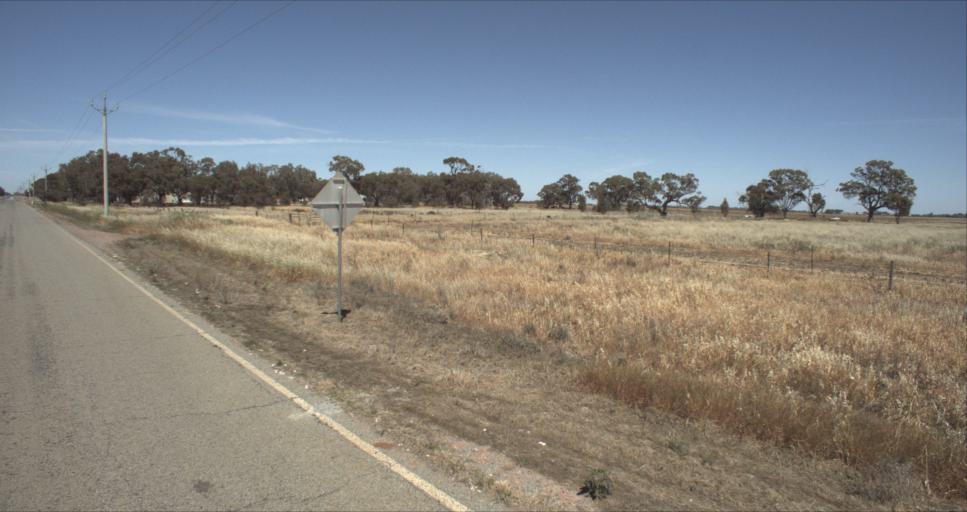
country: AU
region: New South Wales
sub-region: Leeton
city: Leeton
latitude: -34.4947
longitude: 146.2881
